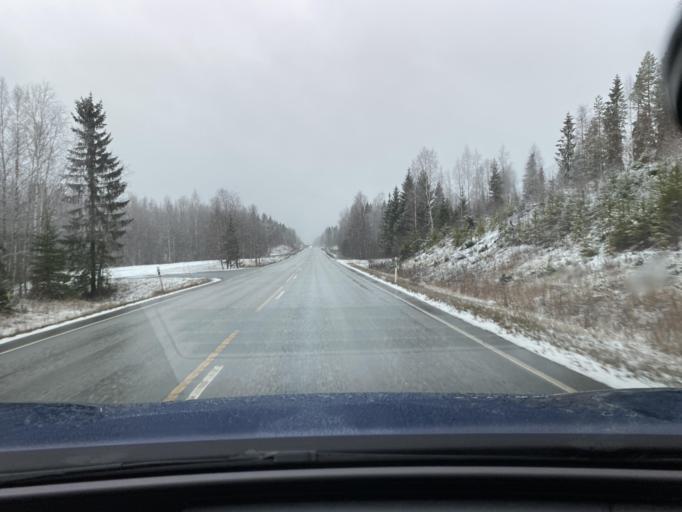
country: FI
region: Northern Ostrobothnia
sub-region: Oulu
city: Kiiminki
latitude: 65.1430
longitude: 25.8761
